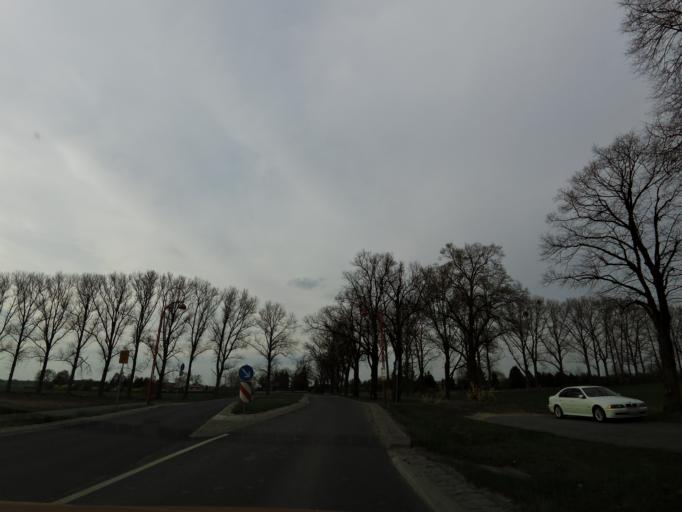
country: DE
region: Brandenburg
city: Mittenwalde
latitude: 52.2738
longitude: 13.5376
